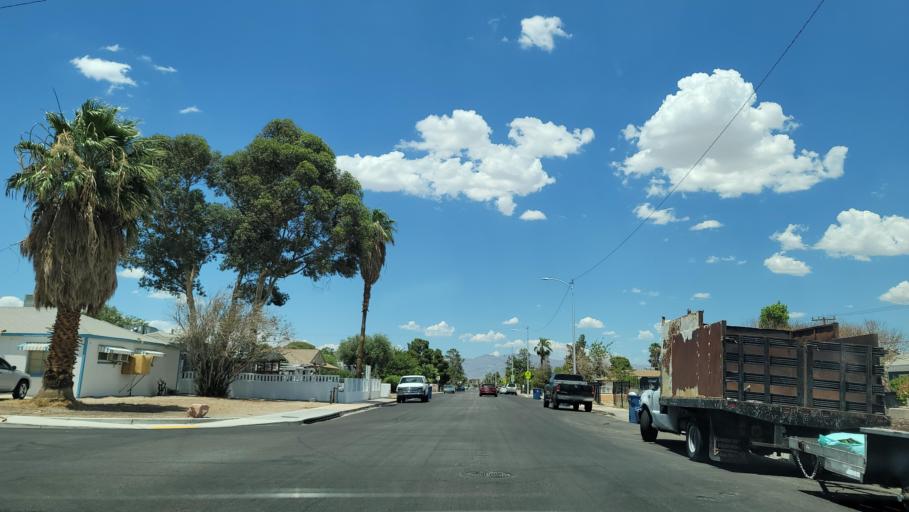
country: US
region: Nevada
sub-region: Clark County
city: Las Vegas
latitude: 36.1610
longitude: -115.1973
